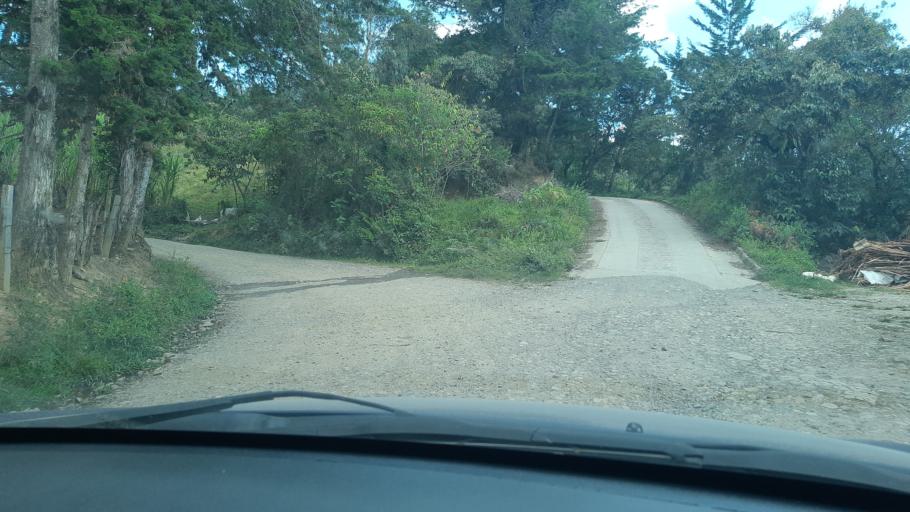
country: CO
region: Boyaca
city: Garagoa
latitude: 5.0869
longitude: -73.3416
